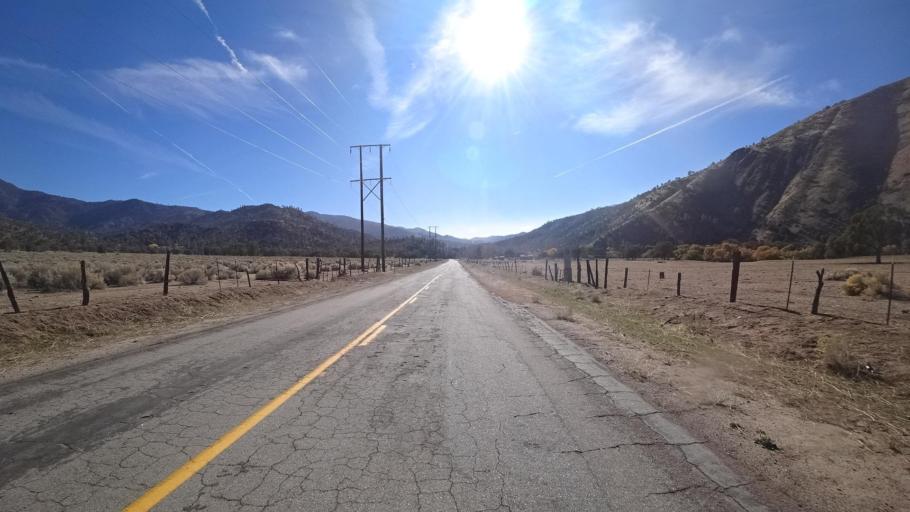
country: US
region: California
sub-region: Kern County
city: Bodfish
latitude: 35.5402
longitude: -118.5104
